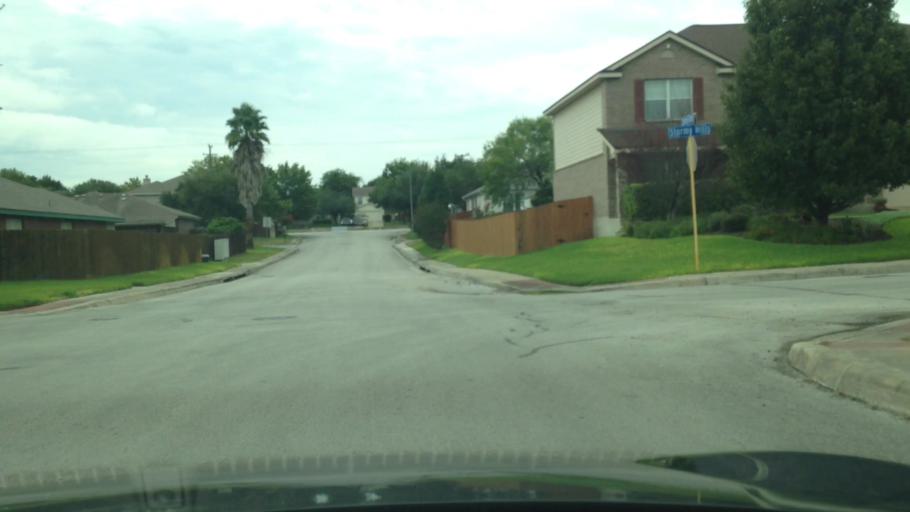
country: US
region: Texas
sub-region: Bexar County
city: Live Oak
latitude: 29.5857
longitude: -98.3835
